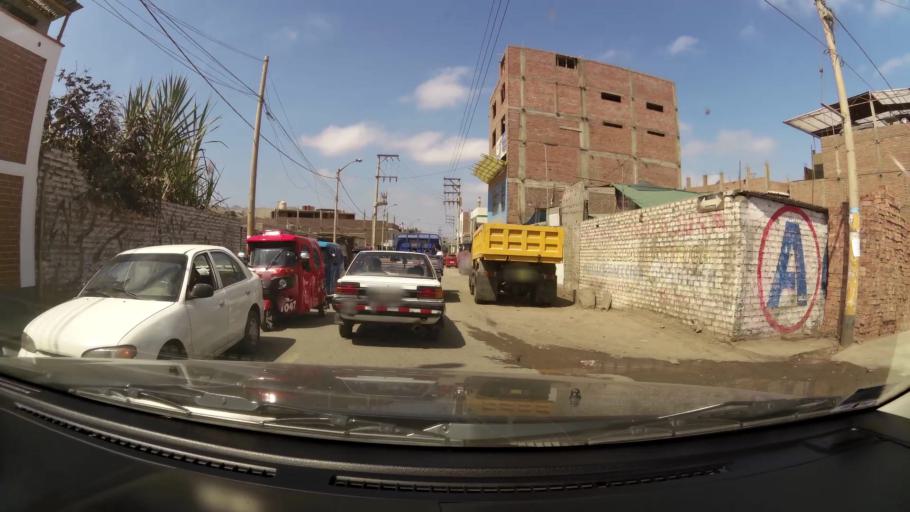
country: PE
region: Lima
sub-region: Provincia de Canete
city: Mala
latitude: -12.6524
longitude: -76.6340
